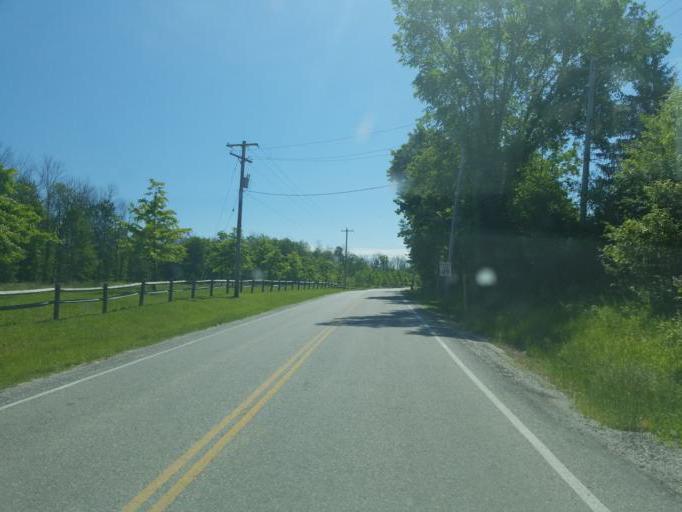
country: US
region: Ohio
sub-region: Summit County
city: Twinsburg
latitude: 41.2860
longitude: -81.3986
